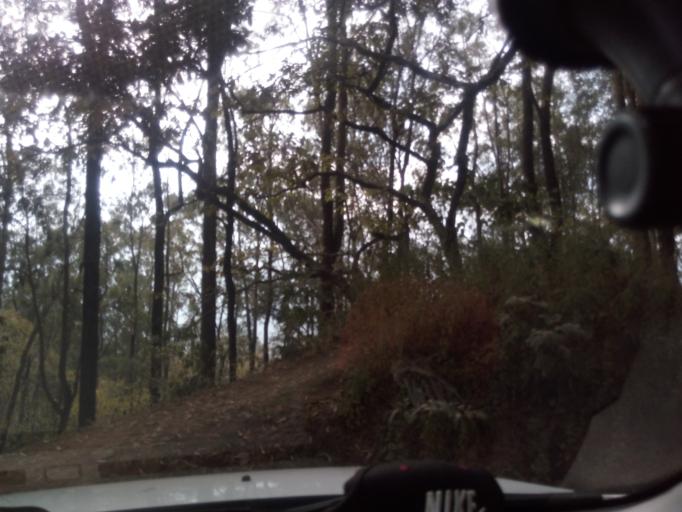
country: GT
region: Sacatepequez
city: Antigua Guatemala
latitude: 14.5654
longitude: -90.7308
